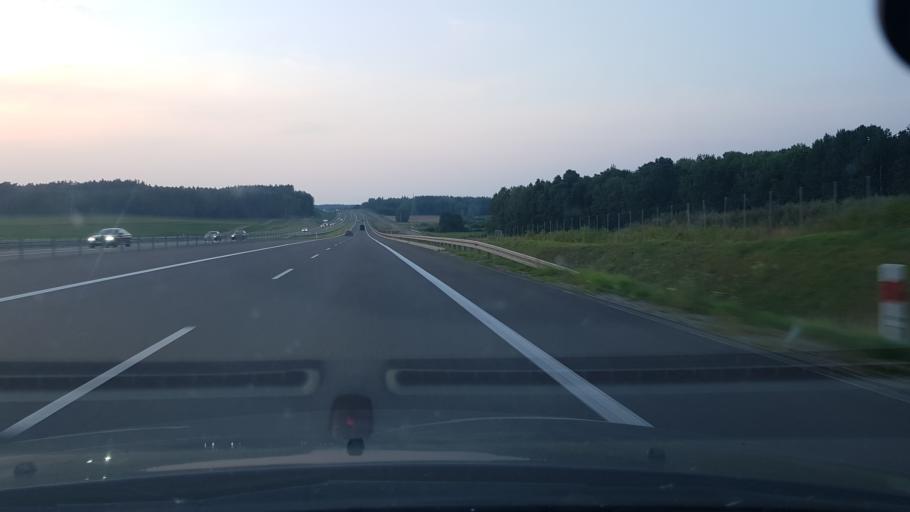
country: PL
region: Warmian-Masurian Voivodeship
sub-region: Powiat nidzicki
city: Nidzica
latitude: 53.3573
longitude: 20.3907
